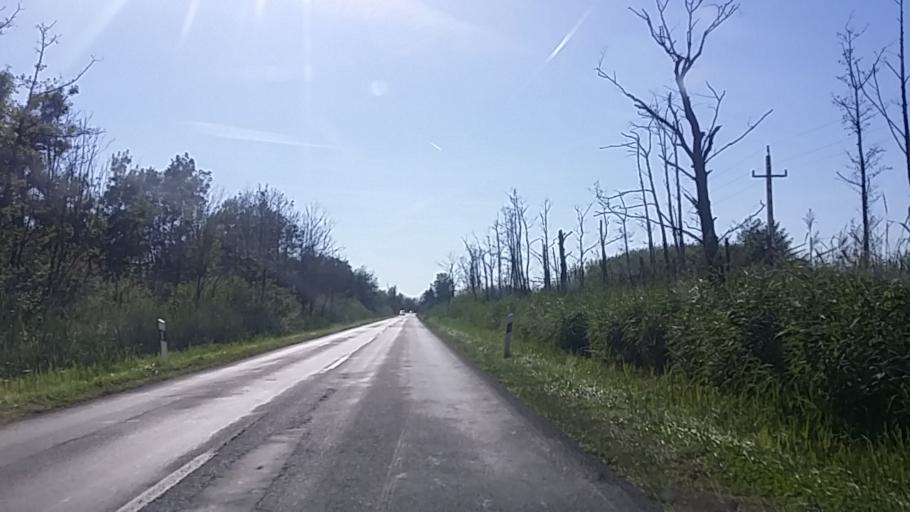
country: HU
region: Zala
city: Sarmellek
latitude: 46.7079
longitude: 17.2131
